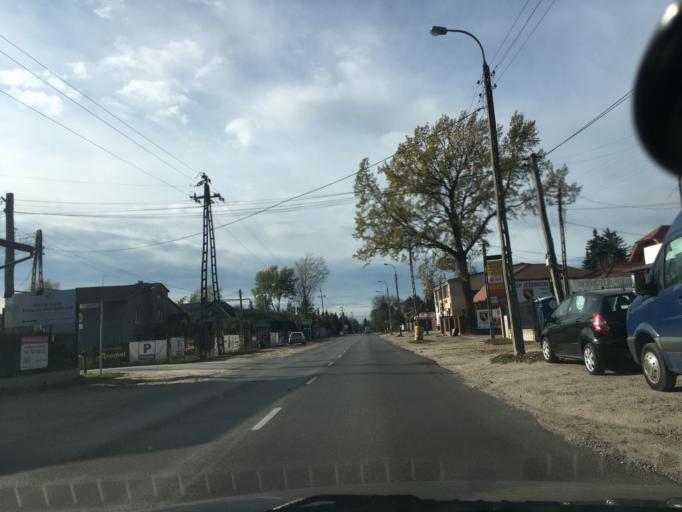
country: PL
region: Masovian Voivodeship
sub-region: Powiat piaseczynski
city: Piaseczno
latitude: 52.0514
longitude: 20.9971
